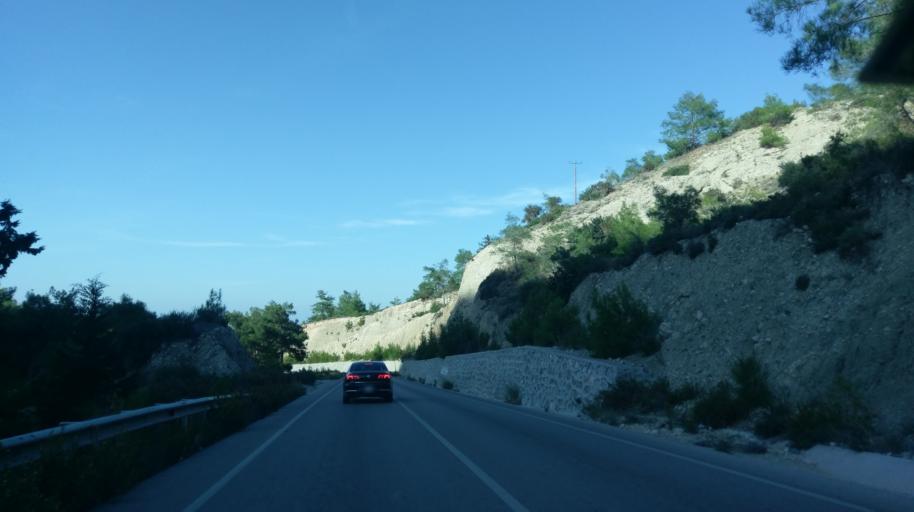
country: CY
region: Ammochostos
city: Lefkonoiko
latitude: 35.3514
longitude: 33.7149
